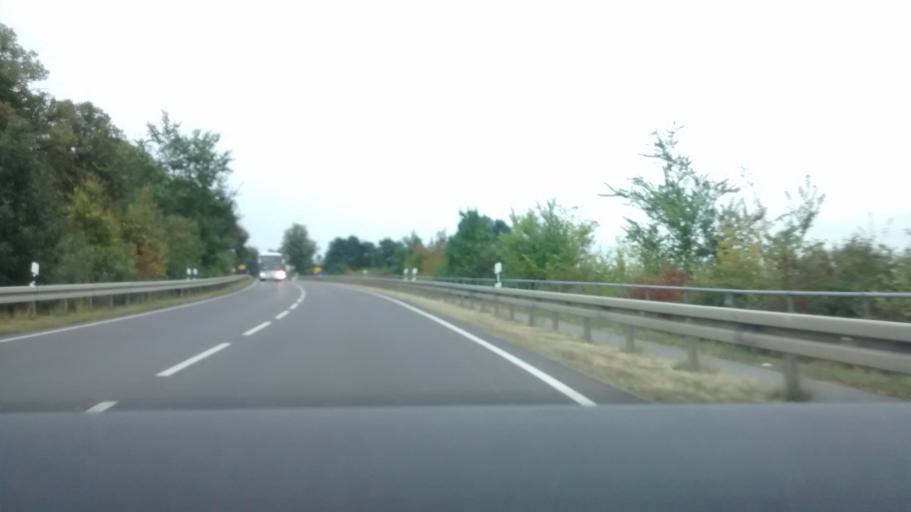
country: DE
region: Mecklenburg-Vorpommern
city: Mecklenburg
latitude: 53.8593
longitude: 11.4523
